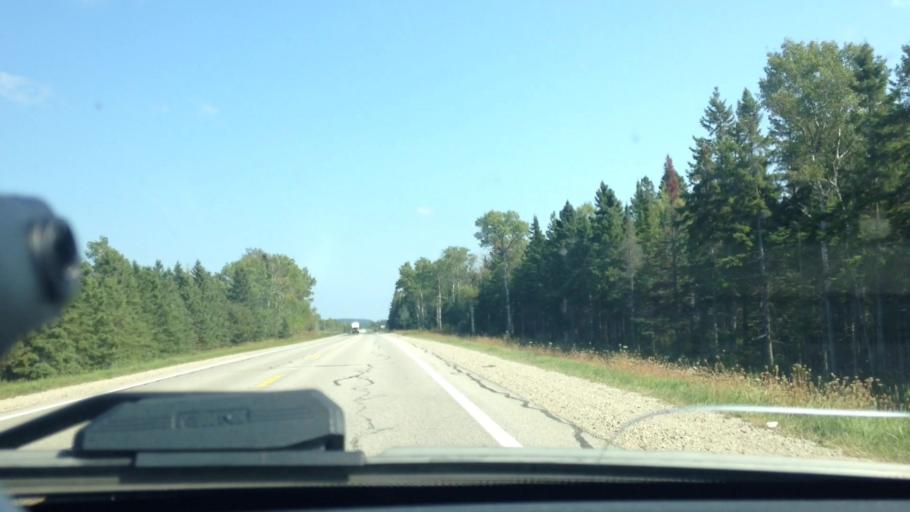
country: US
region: Michigan
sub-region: Luce County
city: Newberry
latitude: 46.3102
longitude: -85.6174
